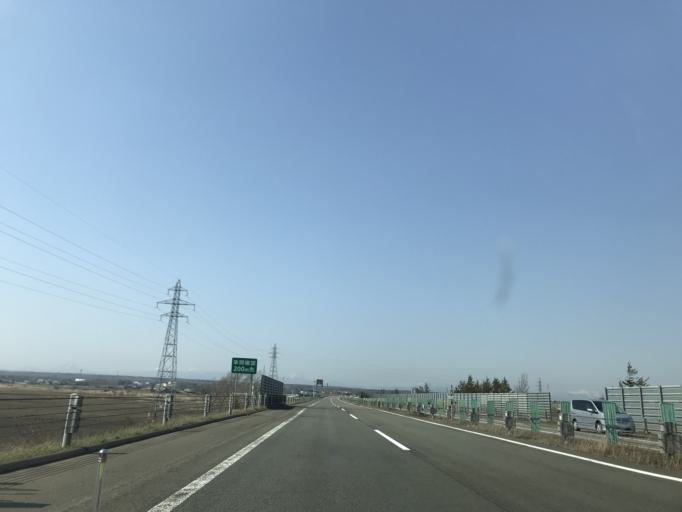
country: JP
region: Hokkaido
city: Ebetsu
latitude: 43.0866
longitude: 141.5640
